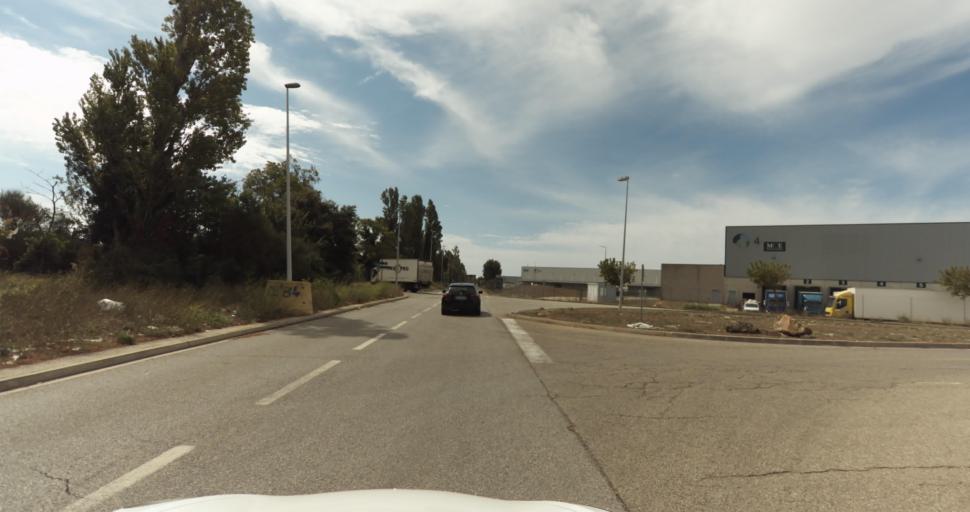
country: FR
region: Provence-Alpes-Cote d'Azur
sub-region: Departement des Bouches-du-Rhone
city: Miramas
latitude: 43.6072
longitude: 5.0004
